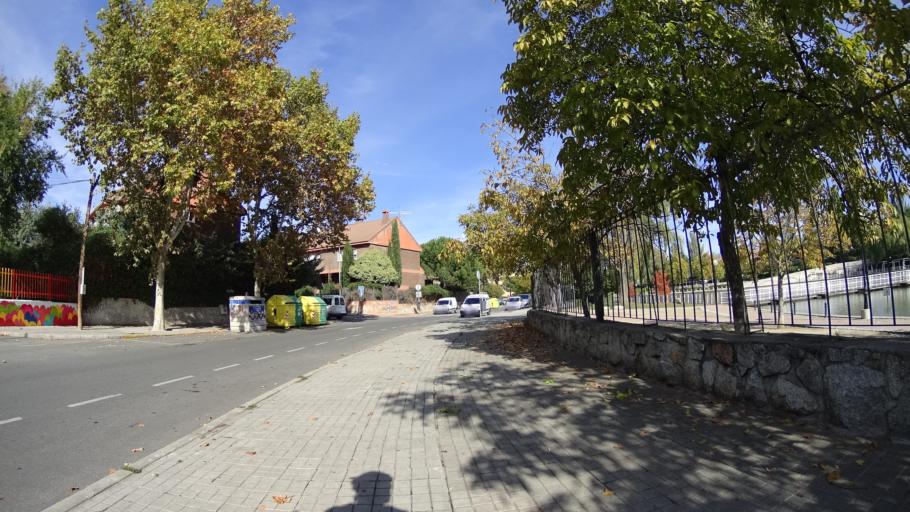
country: ES
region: Madrid
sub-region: Provincia de Madrid
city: Collado-Villalba
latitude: 40.6224
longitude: -4.0180
